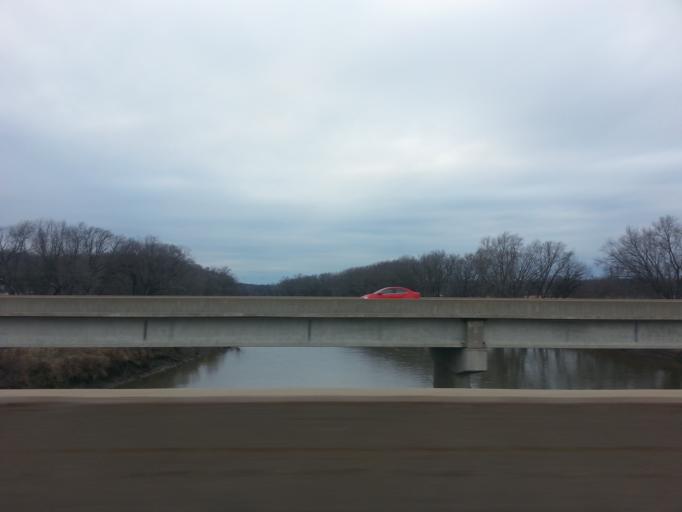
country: US
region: Iowa
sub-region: Henry County
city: Mount Pleasant
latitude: 40.8969
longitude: -91.5550
